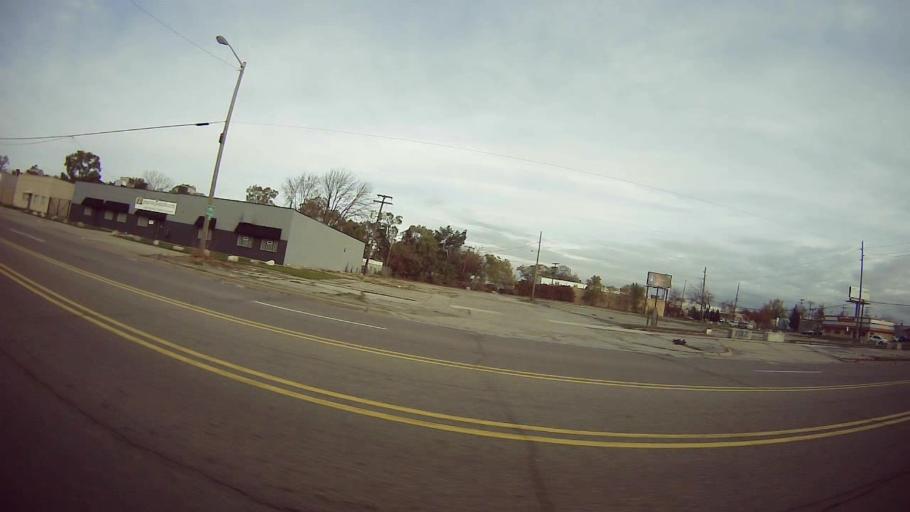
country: US
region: Michigan
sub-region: Oakland County
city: Madison Heights
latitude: 42.4763
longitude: -83.0843
